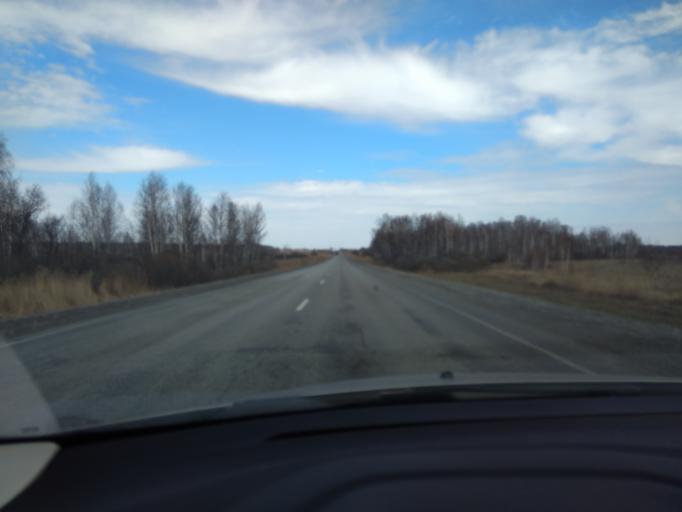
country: RU
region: Sverdlovsk
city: Pyshma
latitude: 56.9883
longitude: 63.2669
